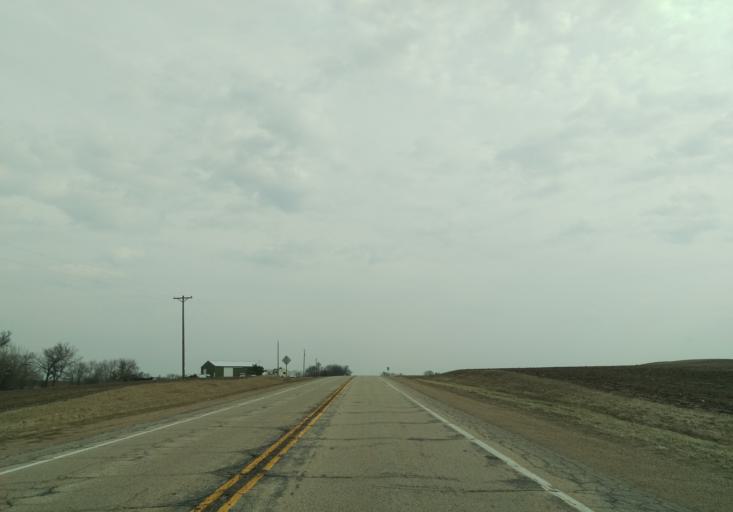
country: US
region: Wisconsin
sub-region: Dane County
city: Waunakee
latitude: 43.1499
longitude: -89.4701
